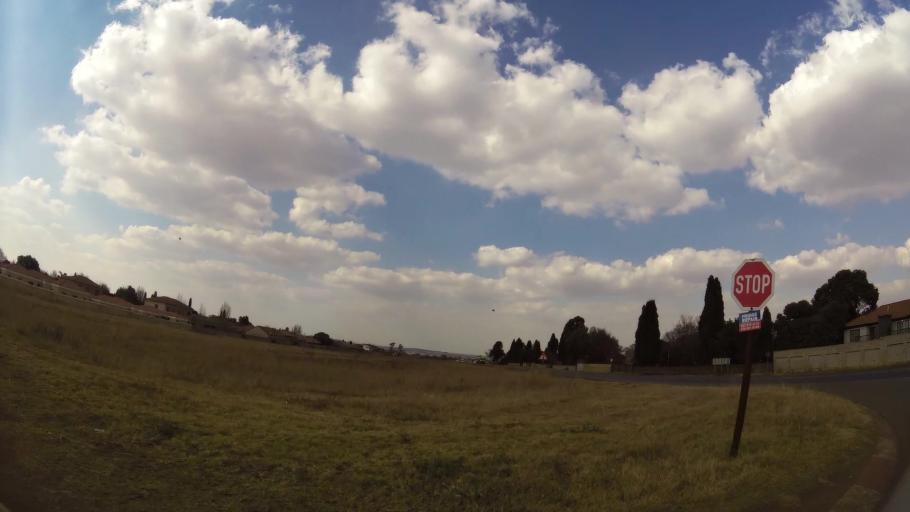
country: ZA
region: Mpumalanga
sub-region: Nkangala District Municipality
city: Delmas
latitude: -26.1399
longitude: 28.6732
